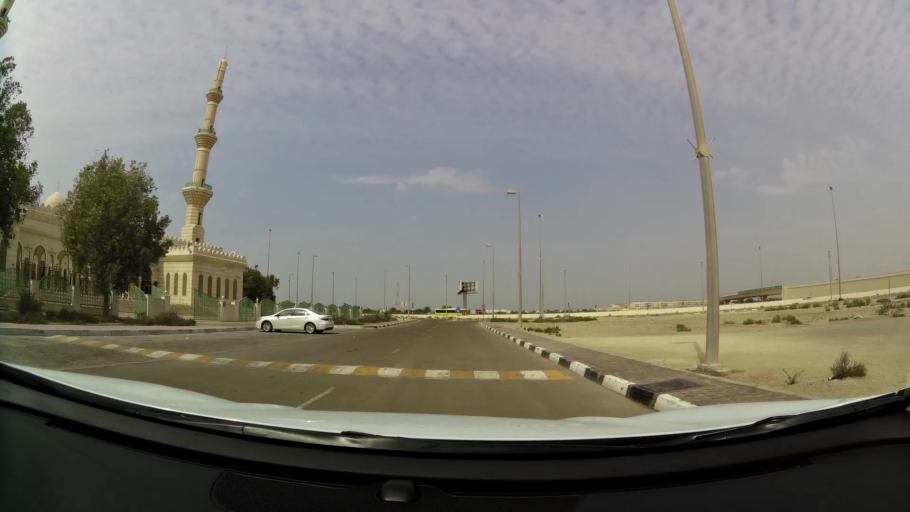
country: AE
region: Abu Dhabi
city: Abu Dhabi
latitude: 24.5419
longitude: 54.6914
